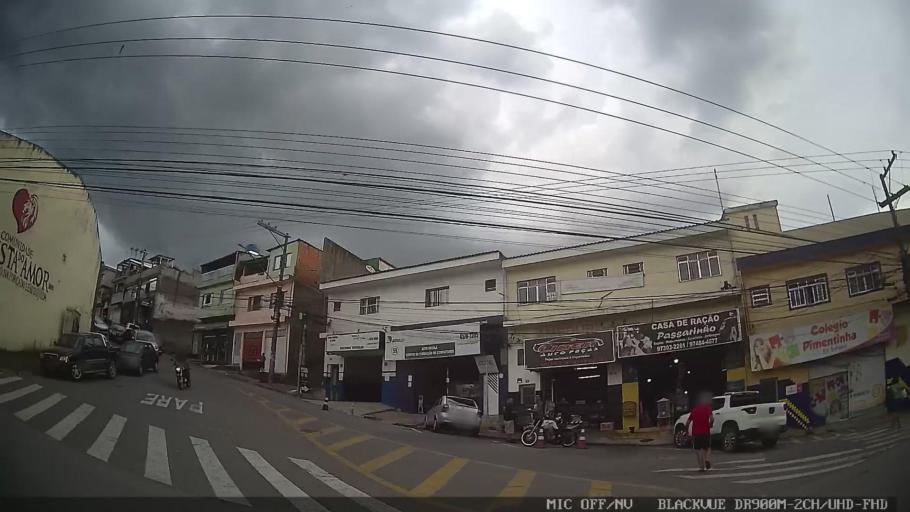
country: BR
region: Sao Paulo
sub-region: Ribeirao Pires
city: Ribeirao Pires
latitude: -23.6755
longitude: -46.4173
